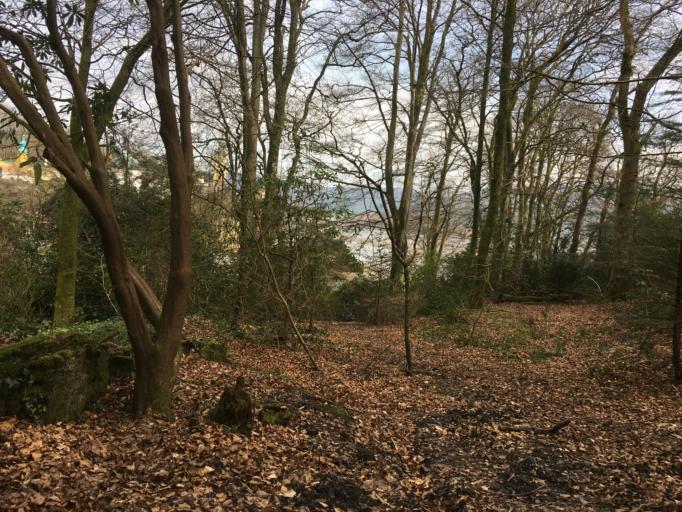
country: GB
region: Wales
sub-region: Gwynedd
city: Porthmadog
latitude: 52.9127
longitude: -4.1004
